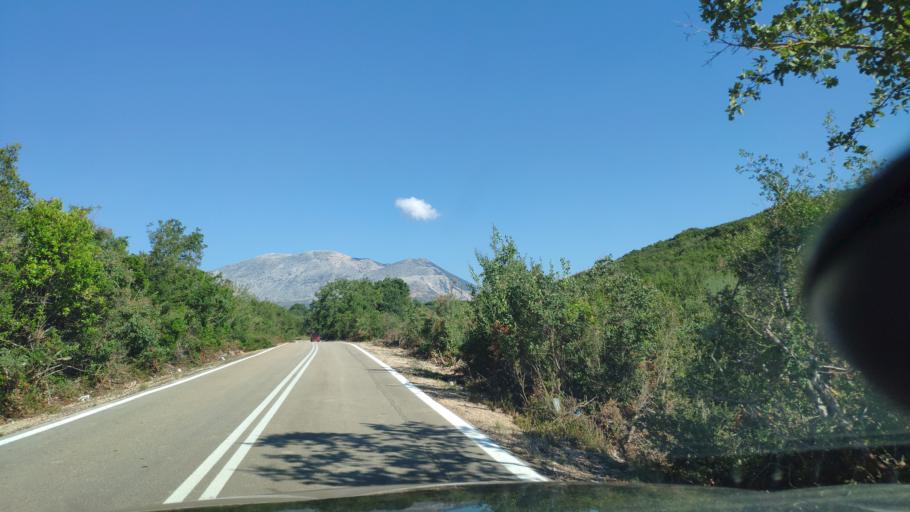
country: GR
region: West Greece
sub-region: Nomos Aitolias kai Akarnanias
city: Fitiai
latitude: 38.6837
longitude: 21.1243
